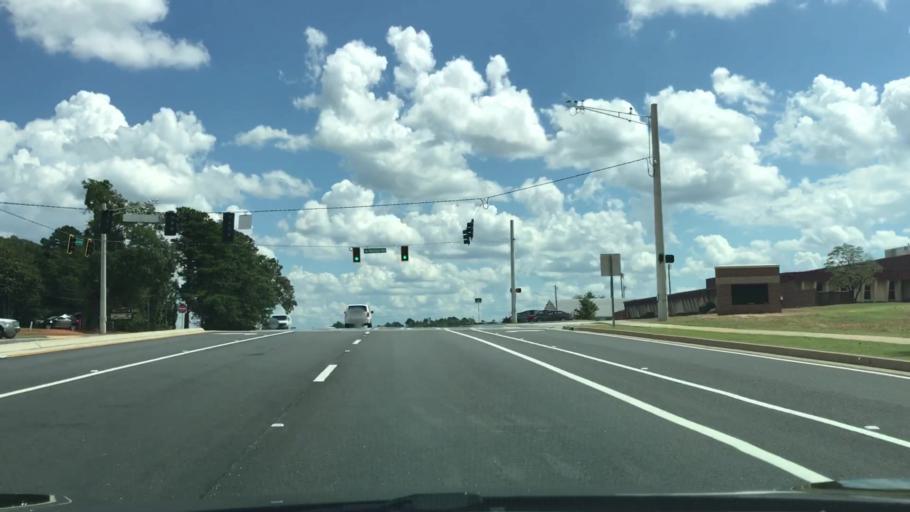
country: US
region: Georgia
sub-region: Oconee County
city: Watkinsville
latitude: 33.8751
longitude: -83.4452
